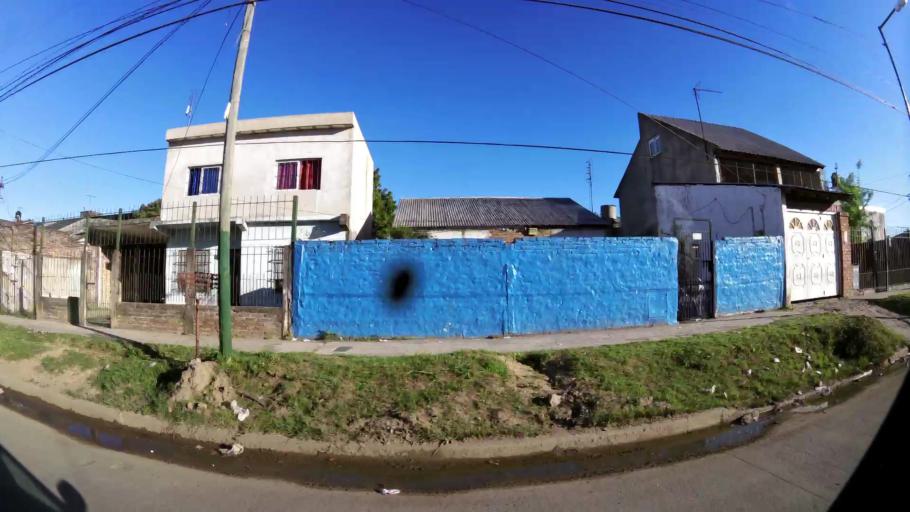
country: AR
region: Buenos Aires
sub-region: Partido de Almirante Brown
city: Adrogue
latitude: -34.7692
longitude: -58.3385
